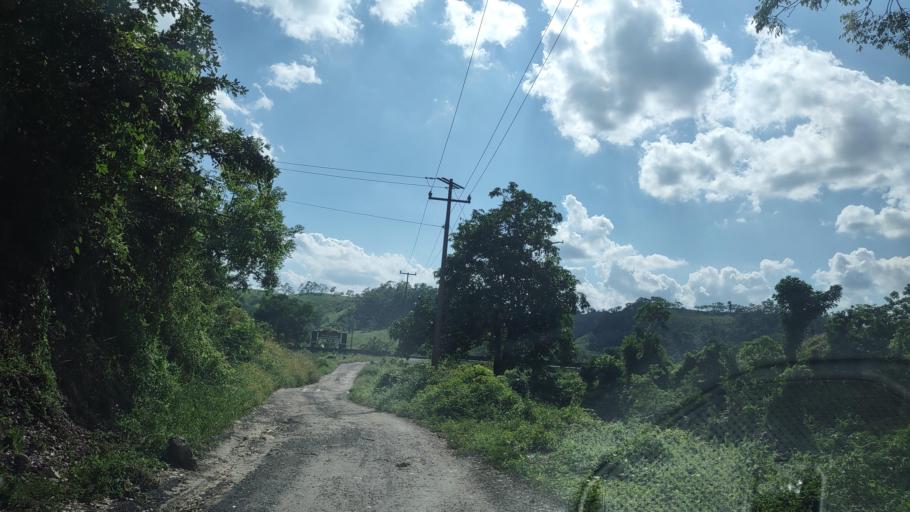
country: MM
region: Shan
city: Taunggyi
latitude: 20.5521
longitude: 97.3425
